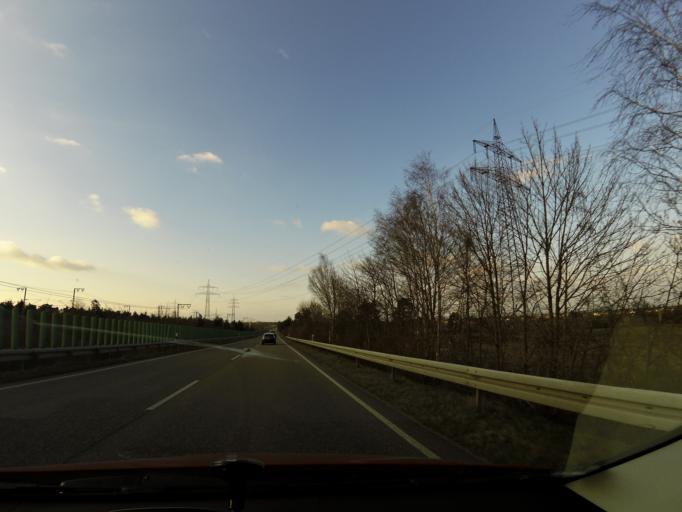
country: DE
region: Baden-Wuerttemberg
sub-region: Karlsruhe Region
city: Waghausel
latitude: 49.2158
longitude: 8.4997
